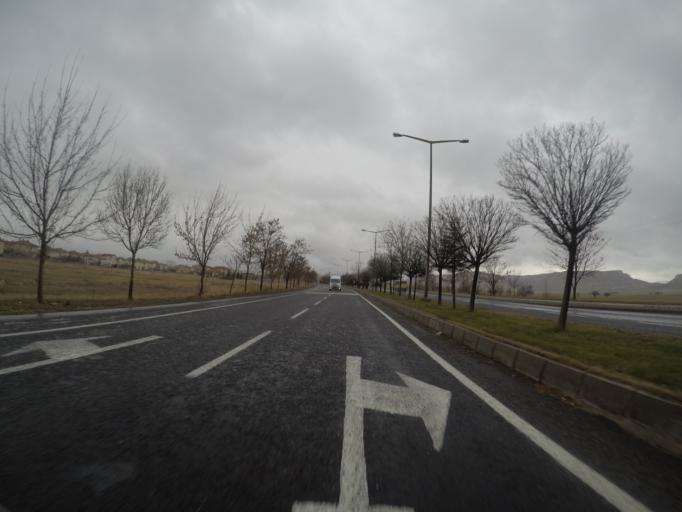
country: TR
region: Nevsehir
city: Avanos
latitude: 38.7029
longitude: 34.8575
